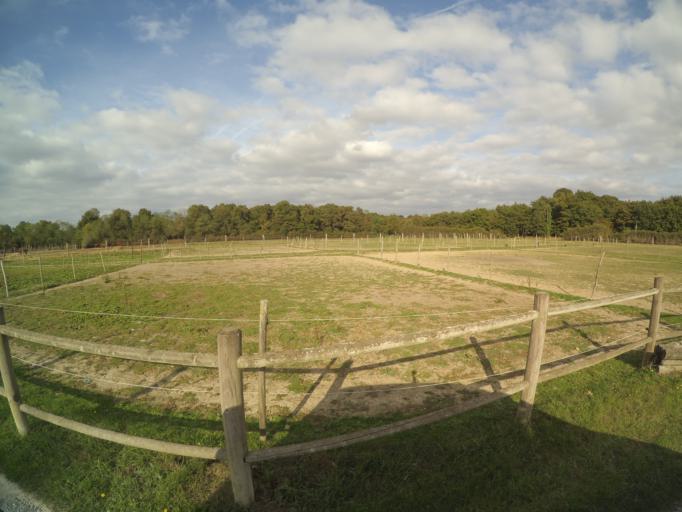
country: FR
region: Centre
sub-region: Departement d'Indre-et-Loire
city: Nazelles-Negron
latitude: 47.4624
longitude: 0.9533
